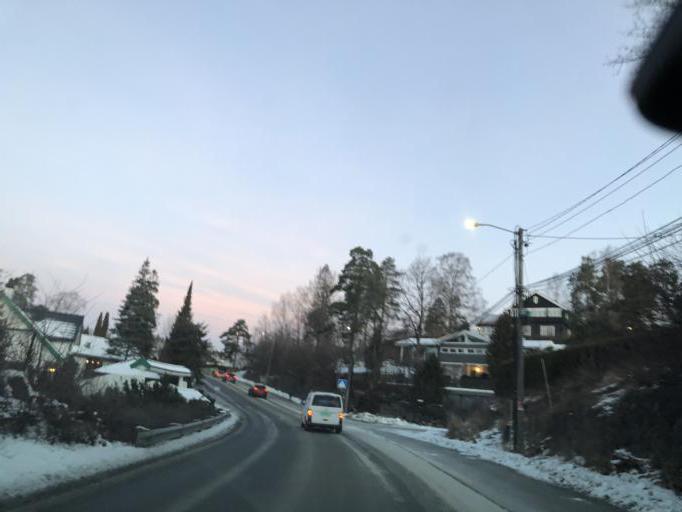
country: NO
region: Akershus
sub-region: Baerum
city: Sandvika
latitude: 59.8733
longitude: 10.5096
